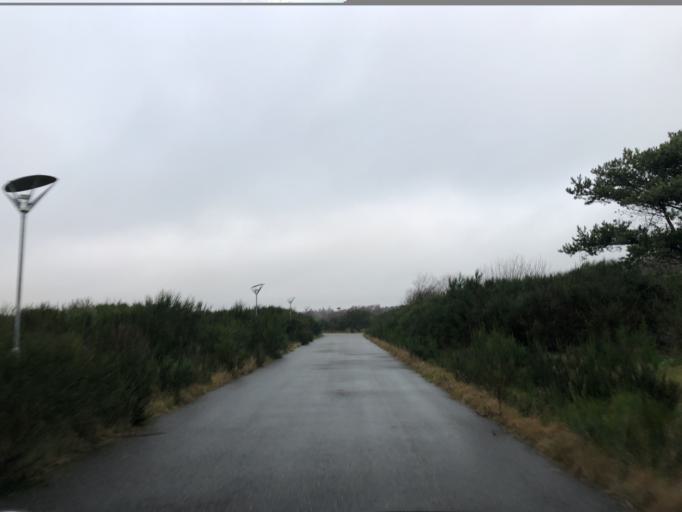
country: DK
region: Central Jutland
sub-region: Holstebro Kommune
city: Ulfborg
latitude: 56.1988
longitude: 8.3071
